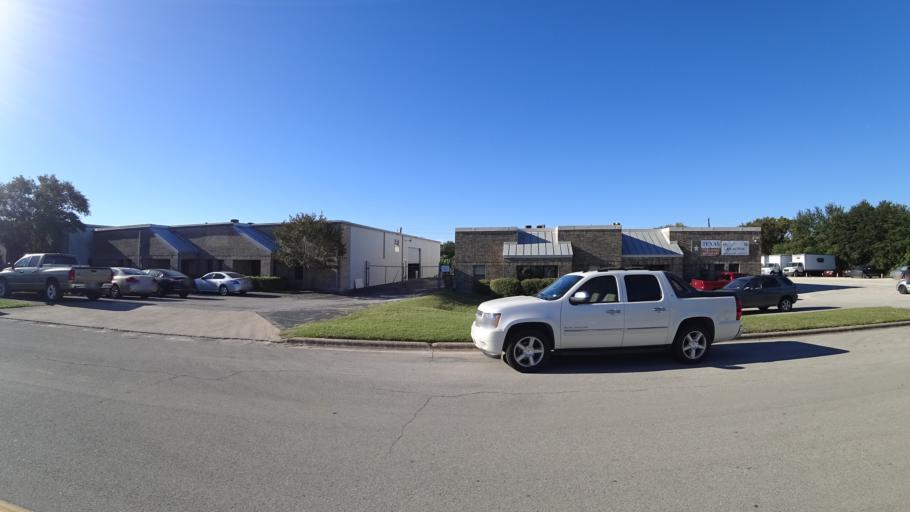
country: US
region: Texas
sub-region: Travis County
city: Manor
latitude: 30.3241
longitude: -97.6560
